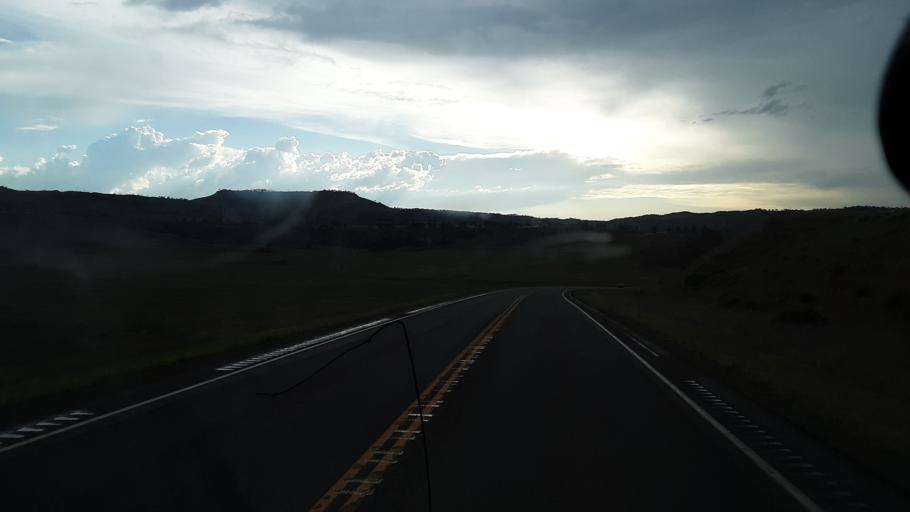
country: US
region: Montana
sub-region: Rosebud County
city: Lame Deer
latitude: 45.6146
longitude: -106.3778
